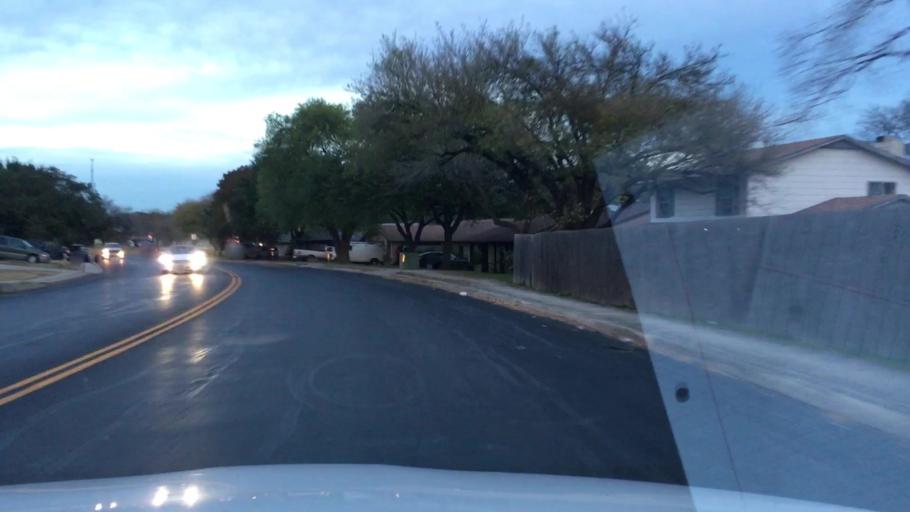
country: US
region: Texas
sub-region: Bexar County
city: Windcrest
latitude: 29.5183
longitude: -98.3555
